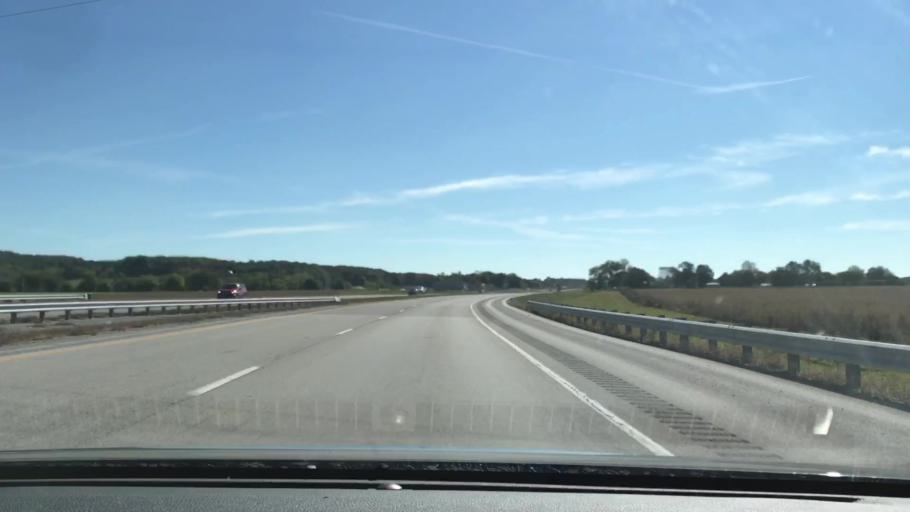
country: US
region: Kentucky
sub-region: Todd County
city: Elkton
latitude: 36.8394
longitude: -87.2444
